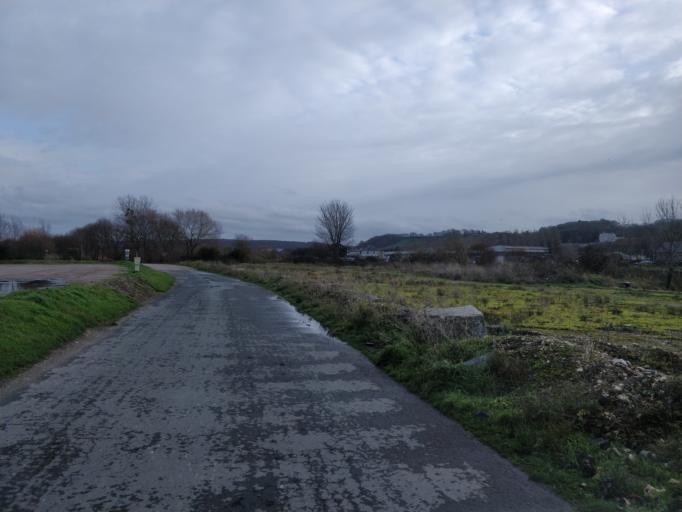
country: FR
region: Lower Normandy
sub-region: Departement du Calvados
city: Honfleur
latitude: 49.4188
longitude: 0.2437
